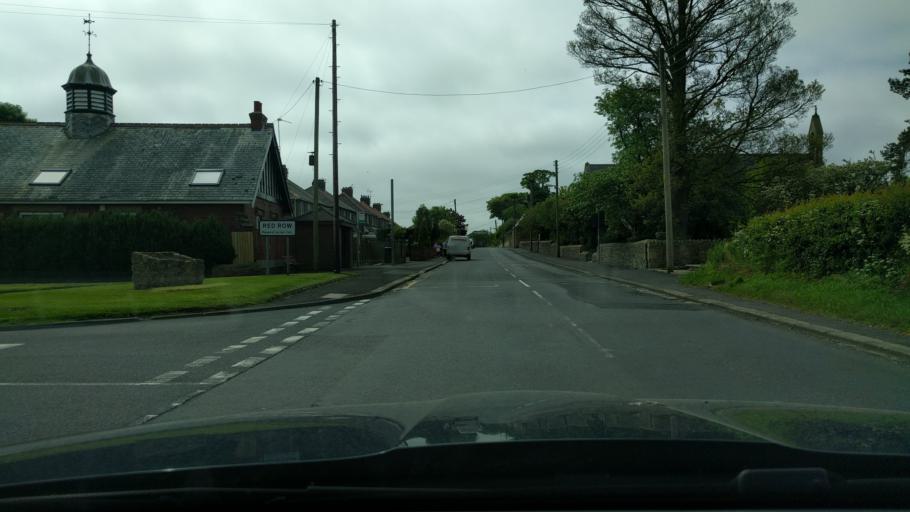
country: GB
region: England
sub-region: Northumberland
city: East Chevington
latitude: 55.2927
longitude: -1.6079
